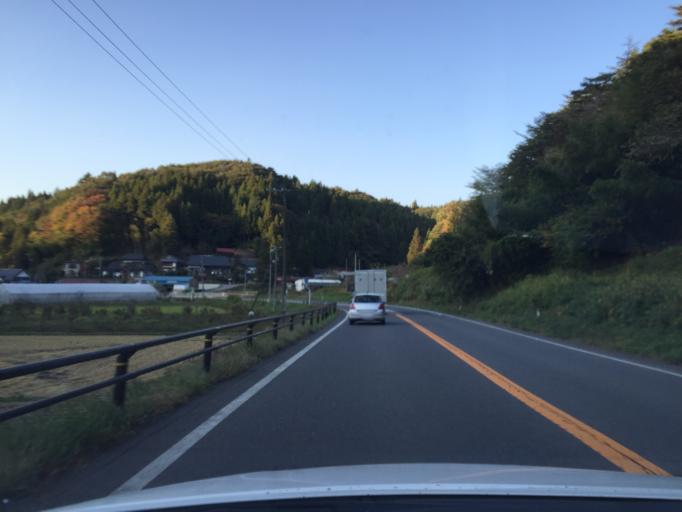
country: JP
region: Fukushima
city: Miharu
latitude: 37.2889
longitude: 140.5428
